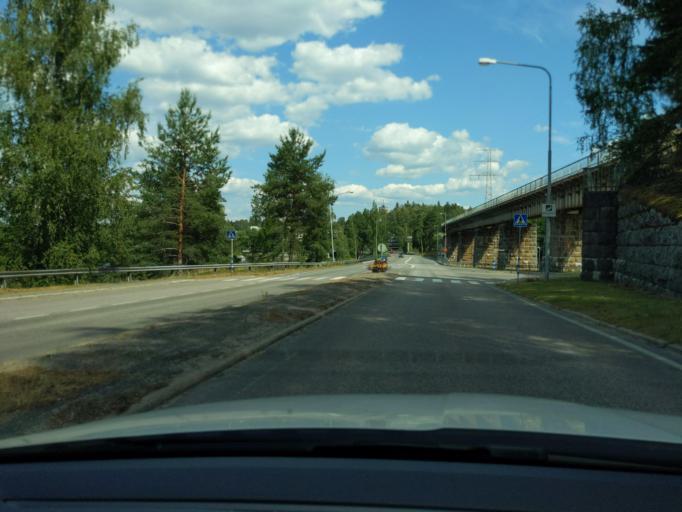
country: FI
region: Paijanne Tavastia
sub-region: Lahti
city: Heinola
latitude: 61.1973
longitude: 26.0283
